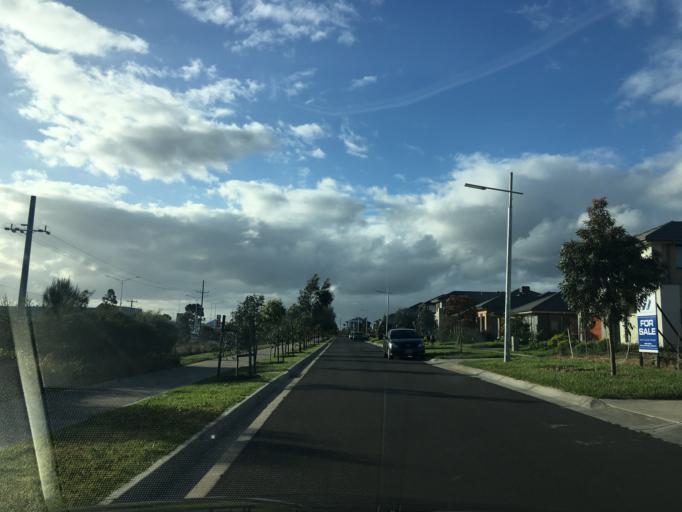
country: AU
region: Victoria
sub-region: Wyndham
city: Williams Landing
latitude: -37.8667
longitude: 144.7347
